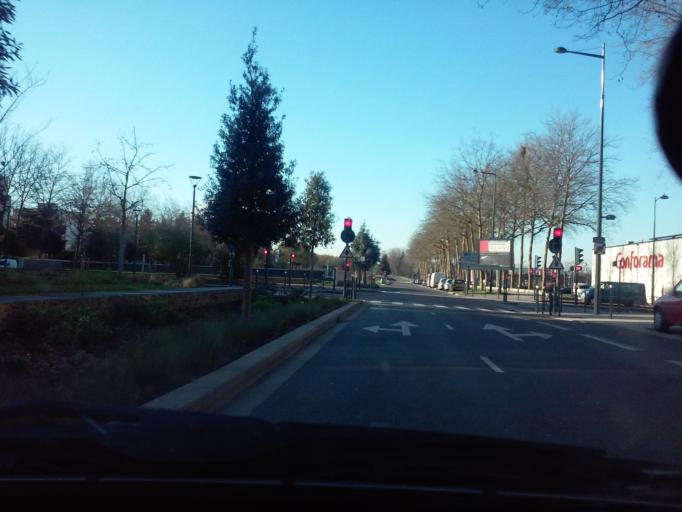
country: FR
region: Brittany
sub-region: Departement d'Ille-et-Vilaine
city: Rennes
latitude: 48.0860
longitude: -1.6750
